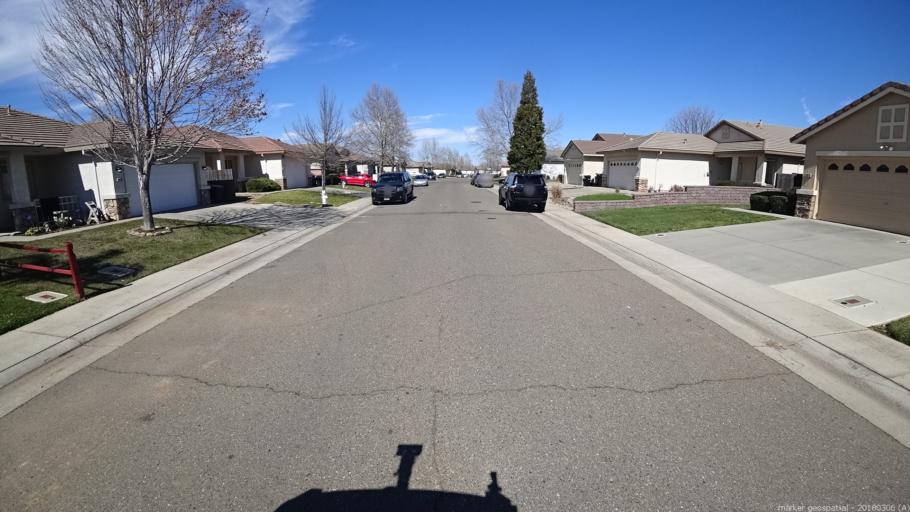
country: US
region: California
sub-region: Sacramento County
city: Vineyard
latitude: 38.4706
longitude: -121.3553
